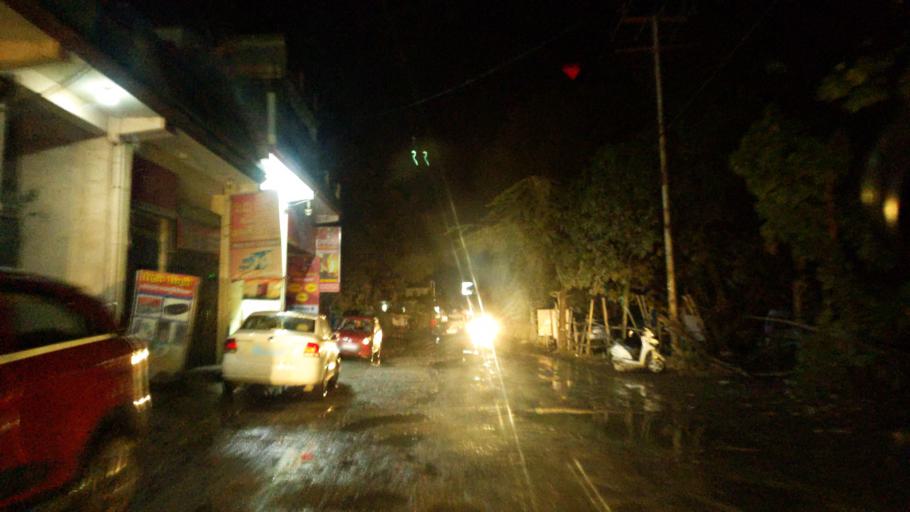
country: IN
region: Uttarakhand
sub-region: Naini Tal
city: Haldwani
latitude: 29.2062
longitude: 79.5166
